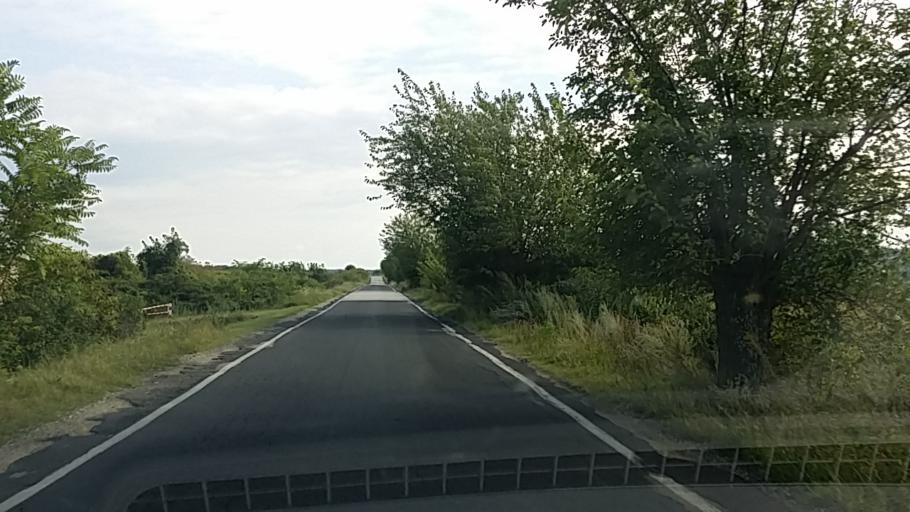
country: HU
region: Gyor-Moson-Sopron
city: Fertorakos
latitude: 47.7499
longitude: 16.6217
